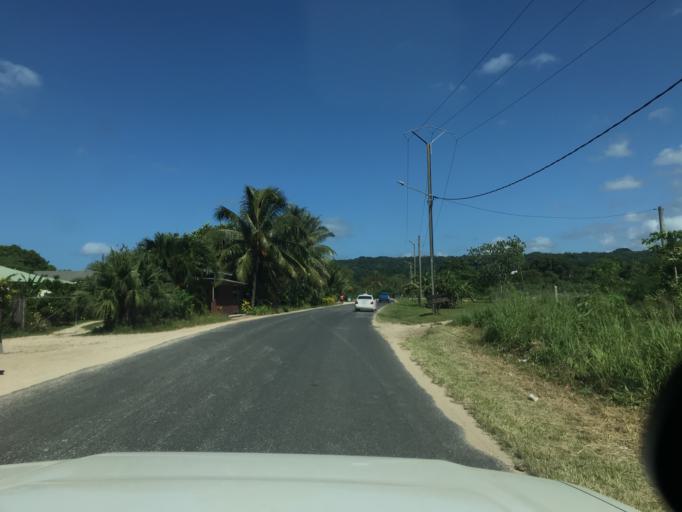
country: VU
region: Sanma
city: Luganville
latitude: -15.5187
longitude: 167.1642
